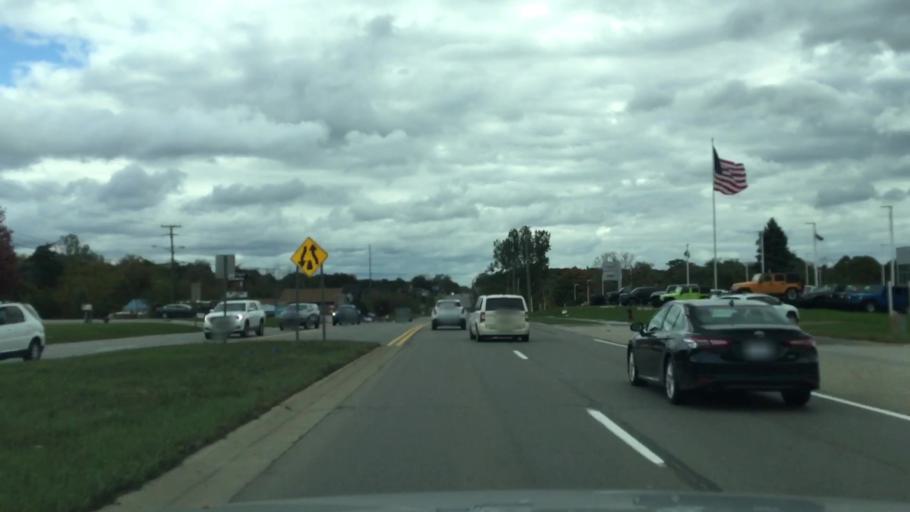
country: US
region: Michigan
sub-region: Oakland County
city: Milford
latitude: 42.6489
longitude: -83.5242
